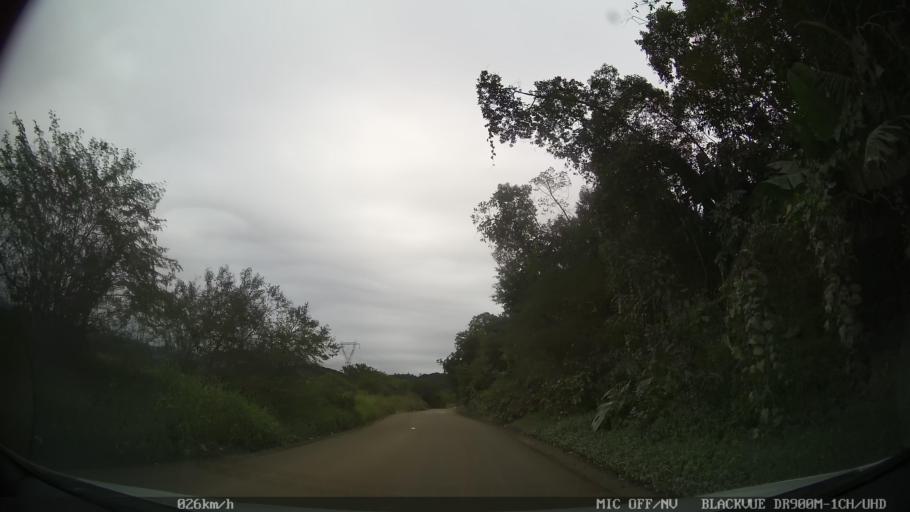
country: BR
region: Santa Catarina
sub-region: Joinville
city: Joinville
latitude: -26.2758
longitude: -48.8906
